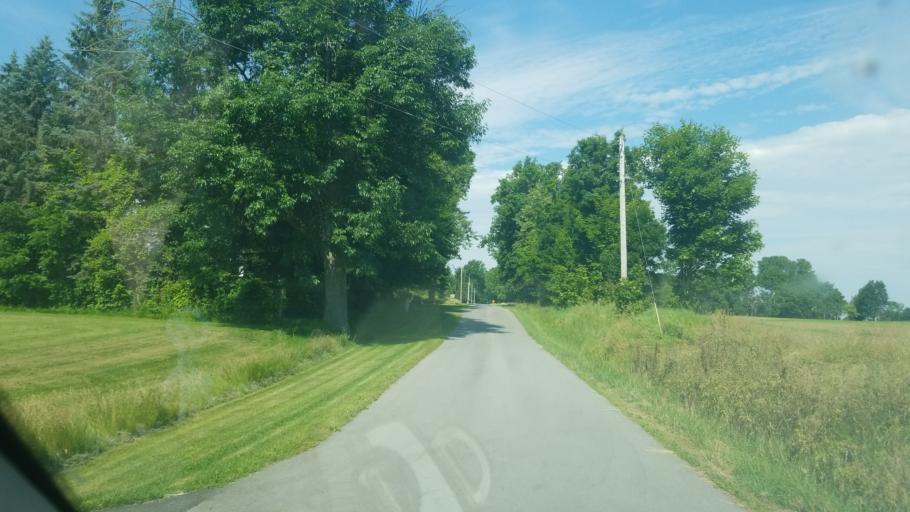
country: US
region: Ohio
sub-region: Wyandot County
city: Carey
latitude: 40.9564
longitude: -83.2949
